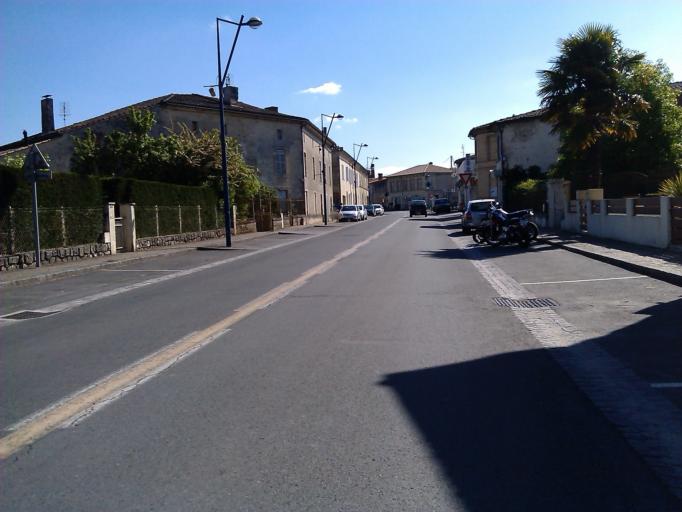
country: FR
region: Aquitaine
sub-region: Departement de la Gironde
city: Cavignac
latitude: 45.1023
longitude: -0.3884
